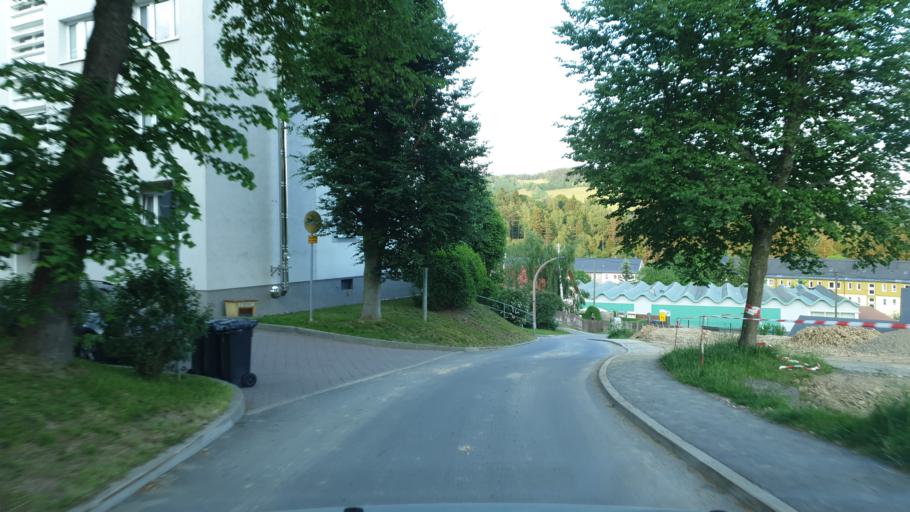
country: DE
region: Saxony
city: Klingenthal
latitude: 50.3604
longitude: 12.4562
